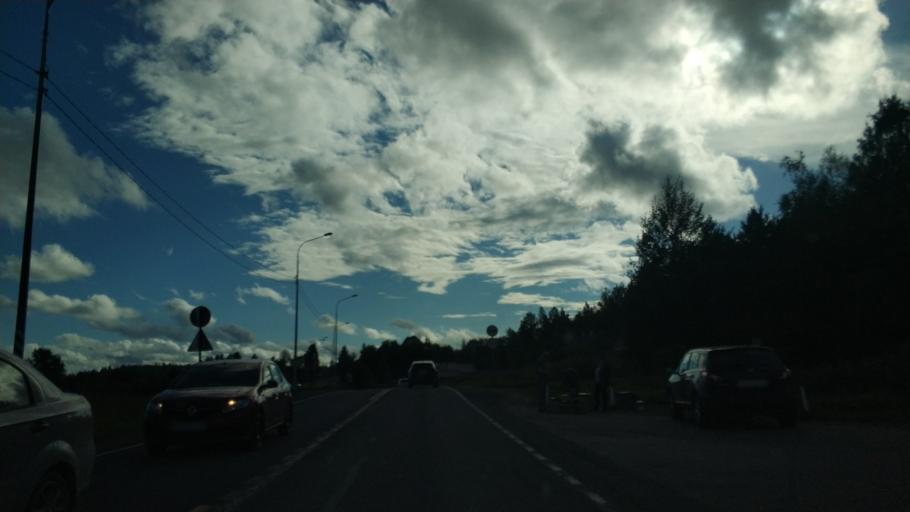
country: RU
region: Republic of Karelia
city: Lakhdenpokh'ya
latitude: 61.5553
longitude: 30.3233
